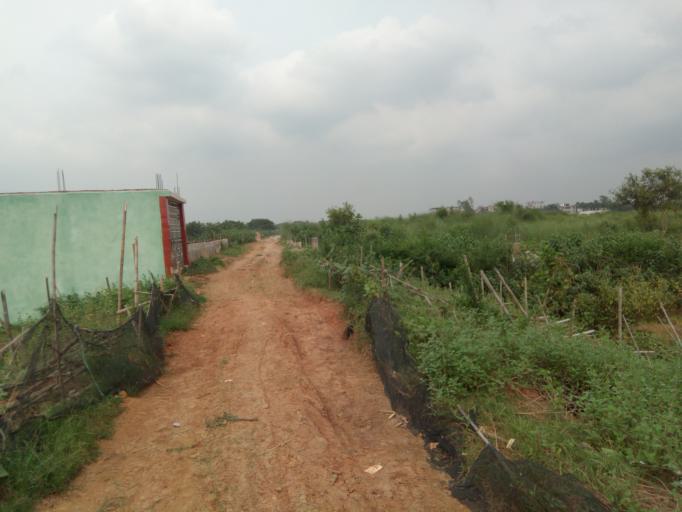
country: BD
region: Dhaka
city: Paltan
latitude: 23.7389
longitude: 90.4720
